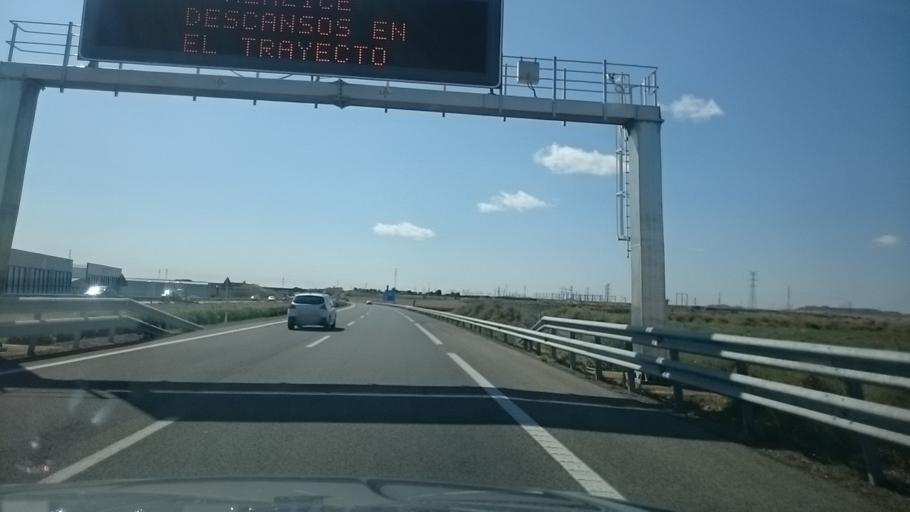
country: ES
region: Aragon
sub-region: Provincia de Zaragoza
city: Mallen
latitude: 41.8600
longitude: -1.3874
